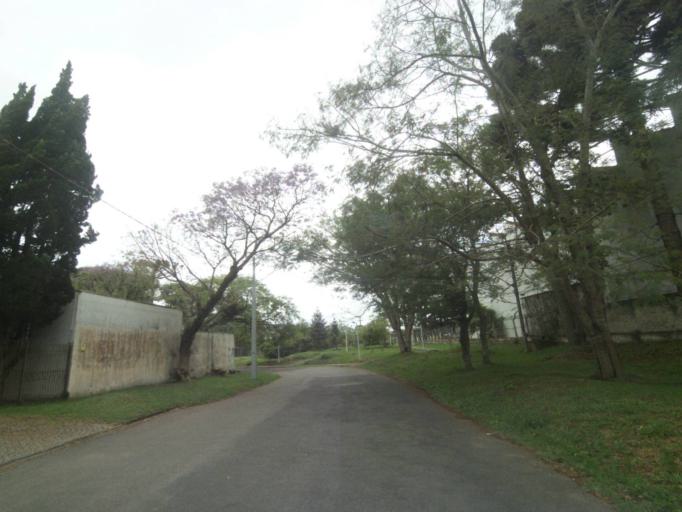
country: BR
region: Parana
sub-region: Pinhais
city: Pinhais
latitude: -25.4203
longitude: -49.2262
